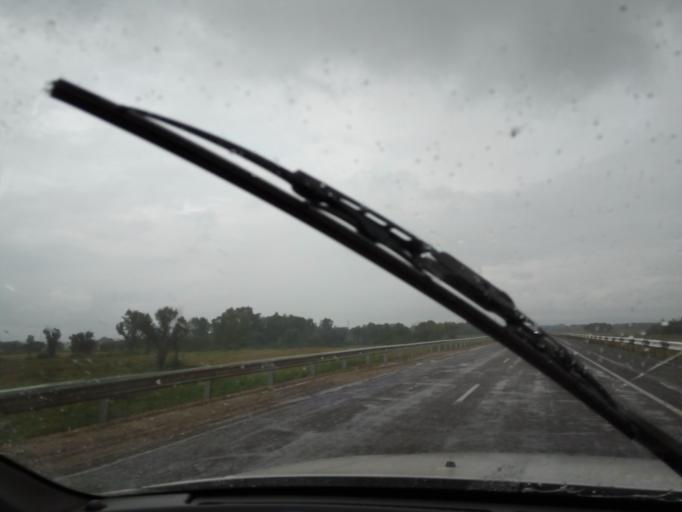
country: RU
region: Primorskiy
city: Dal'nerechensk
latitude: 45.9114
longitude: 133.7638
